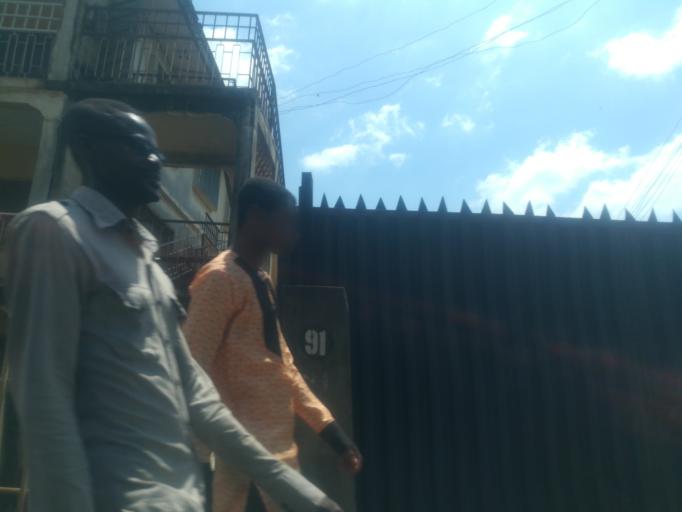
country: NG
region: Oyo
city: Ibadan
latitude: 7.3621
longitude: 3.8728
